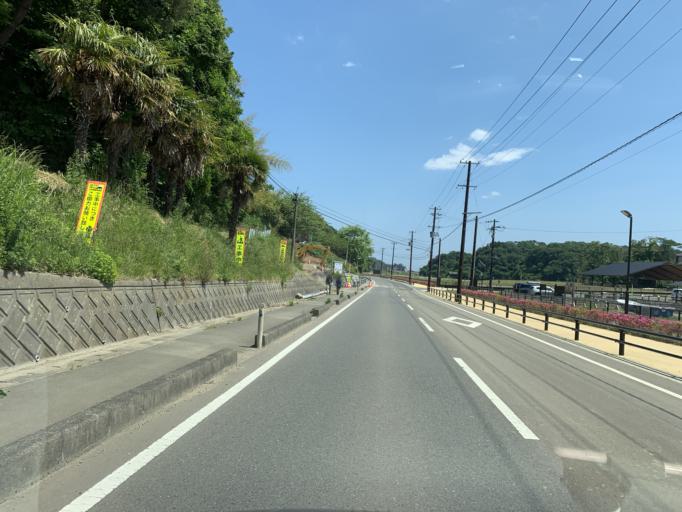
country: JP
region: Miyagi
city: Matsushima
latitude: 38.3347
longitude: 141.1550
